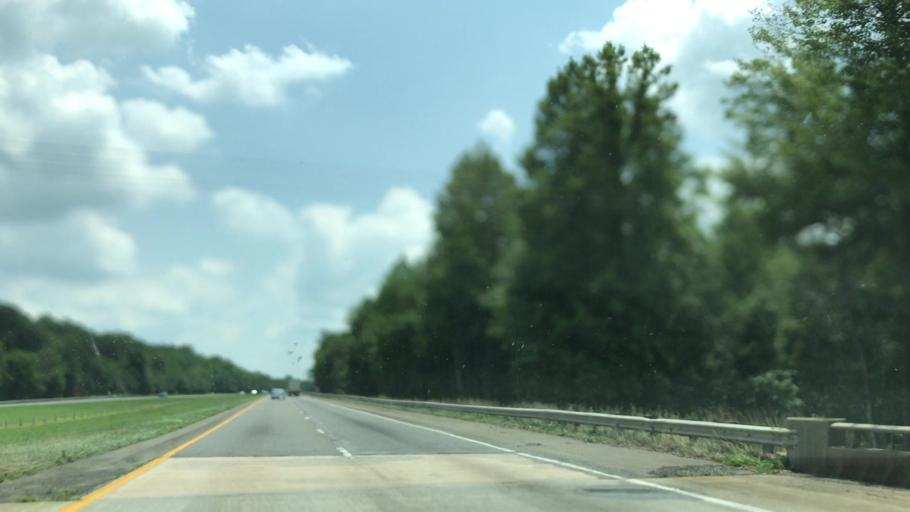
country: US
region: North Carolina
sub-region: Surry County
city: Dobson
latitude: 36.3346
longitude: -80.7943
